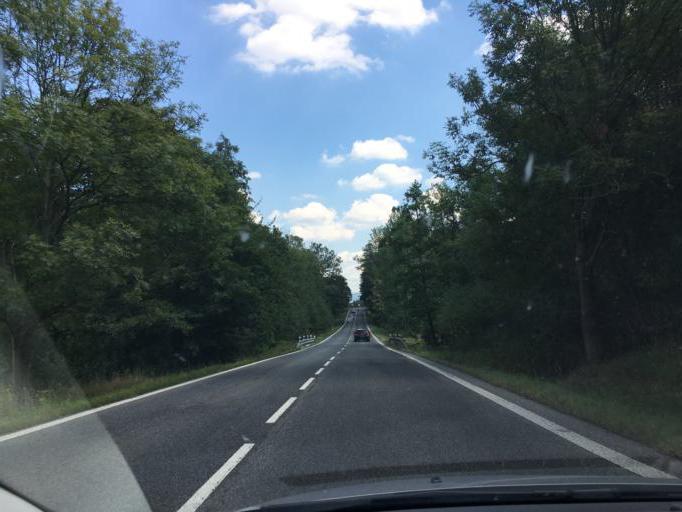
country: CZ
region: Ustecky
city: Benesov nad Ploucnici
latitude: 50.7903
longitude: 14.3190
